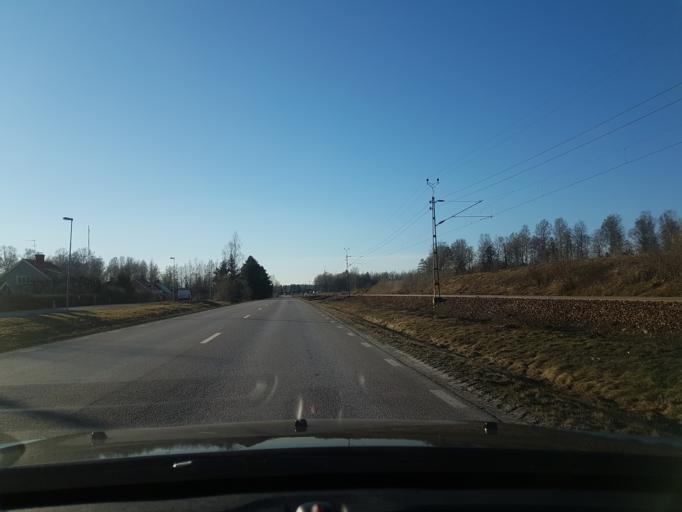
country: SE
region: Uppsala
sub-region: Heby Kommun
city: Morgongava
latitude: 59.9266
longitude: 16.9806
